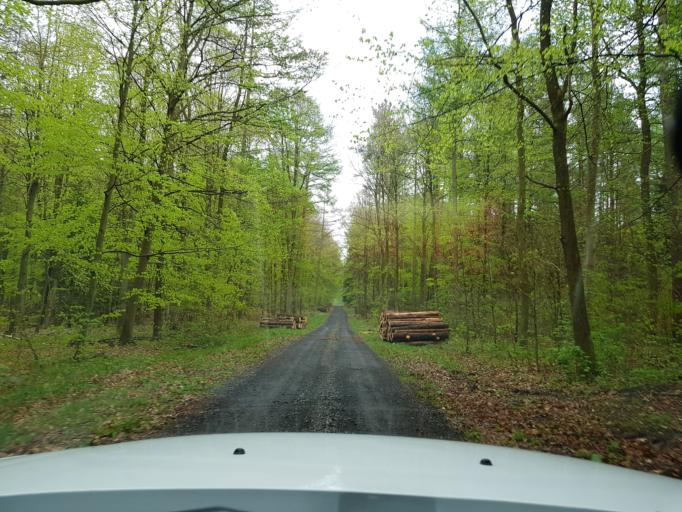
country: PL
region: West Pomeranian Voivodeship
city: Trzcinsko Zdroj
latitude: 52.9963
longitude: 14.6464
